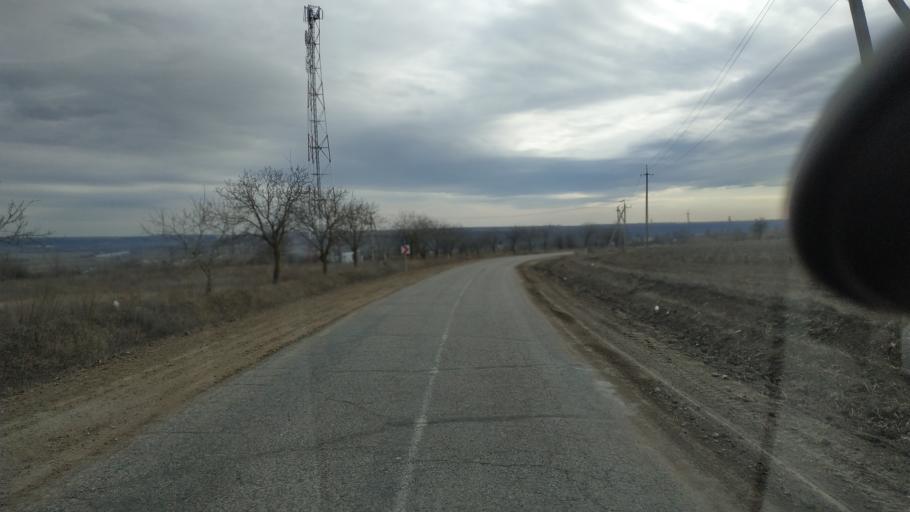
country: MD
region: Telenesti
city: Cocieri
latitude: 47.2695
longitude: 29.1142
